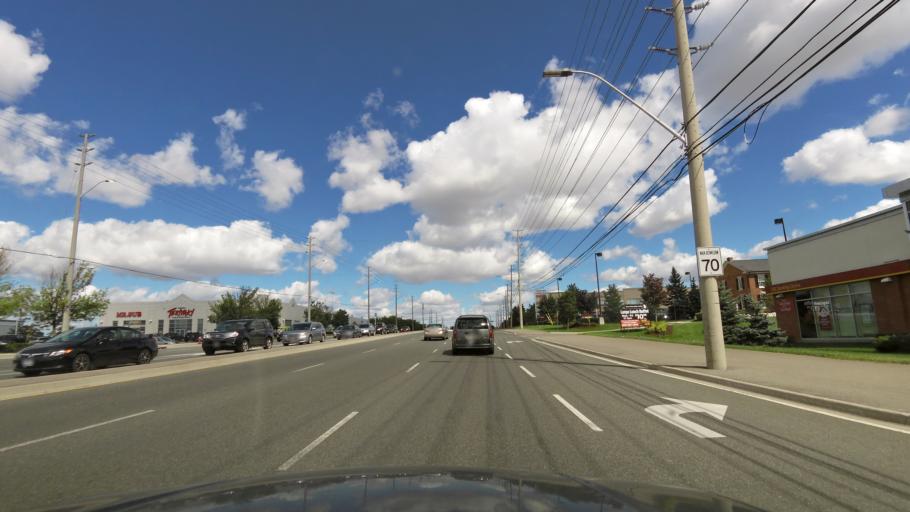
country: CA
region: Ontario
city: Mississauga
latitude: 43.6092
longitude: -79.6988
